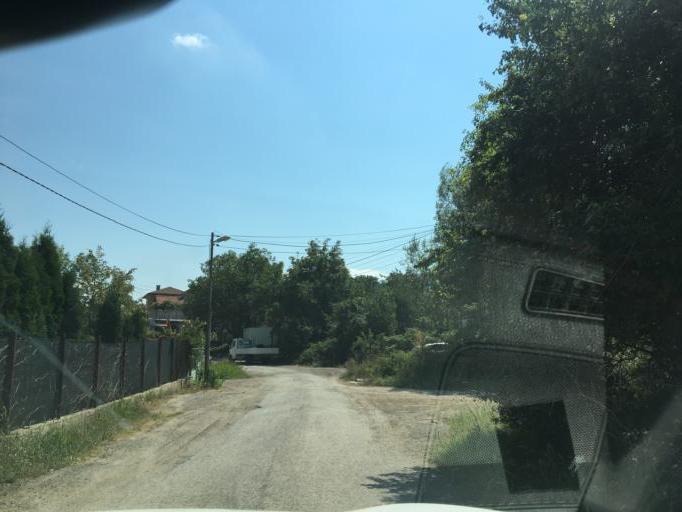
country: BG
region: Sofiya
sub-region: Obshtina Elin Pelin
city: Elin Pelin
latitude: 42.6072
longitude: 23.4672
